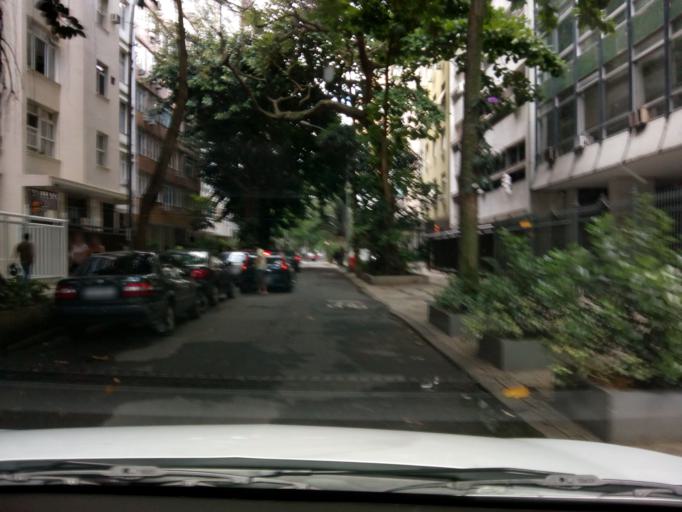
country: BR
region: Rio de Janeiro
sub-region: Rio De Janeiro
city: Rio de Janeiro
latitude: -22.9713
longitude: -43.1910
